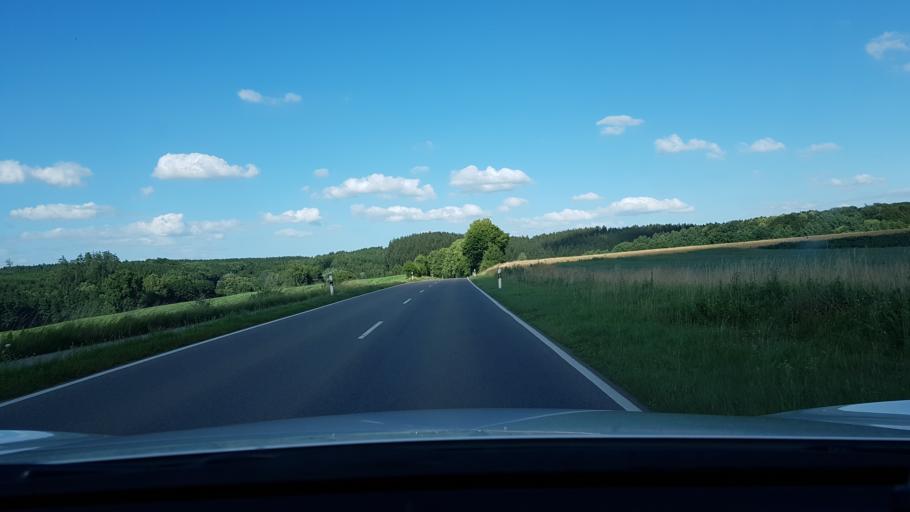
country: DE
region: Baden-Wuerttemberg
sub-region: Tuebingen Region
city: Schwendi
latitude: 48.1795
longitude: 9.9828
